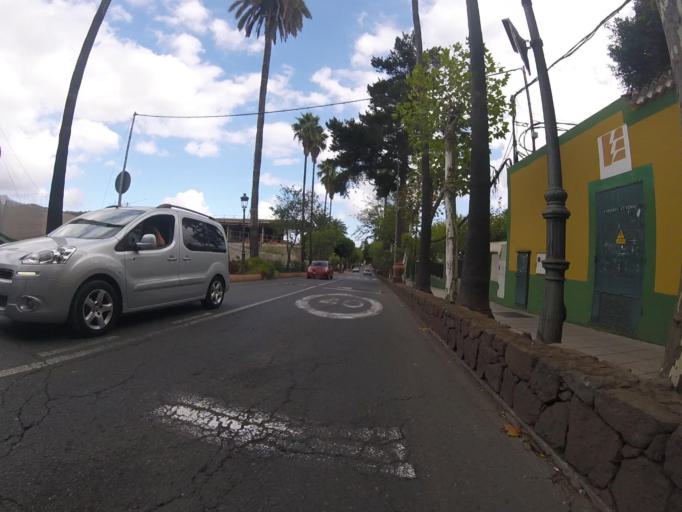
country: ES
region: Canary Islands
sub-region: Provincia de Las Palmas
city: Santa Brigida
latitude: 28.0334
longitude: -15.4980
